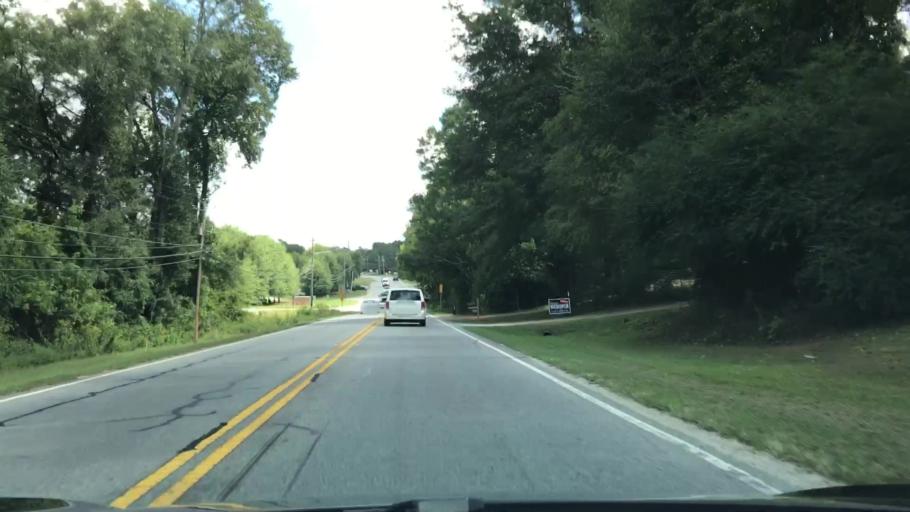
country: US
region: Georgia
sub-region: Oconee County
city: Watkinsville
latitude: 33.8682
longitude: -83.4171
